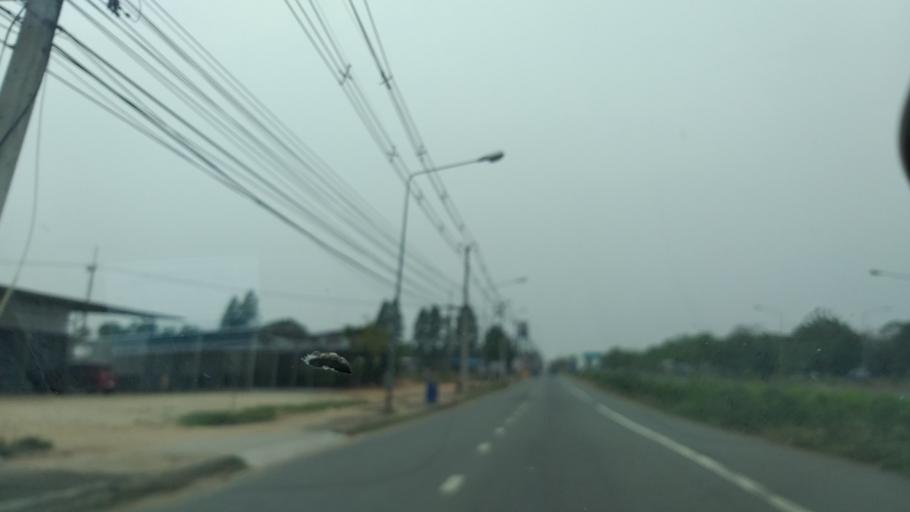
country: TH
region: Chon Buri
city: Ko Chan
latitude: 13.4807
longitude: 101.2807
